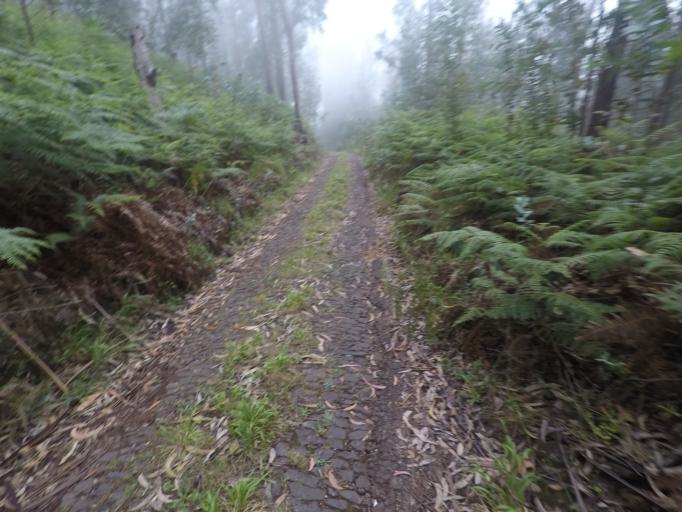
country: PT
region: Madeira
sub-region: Calheta
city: Arco da Calheta
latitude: 32.7244
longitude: -17.0941
